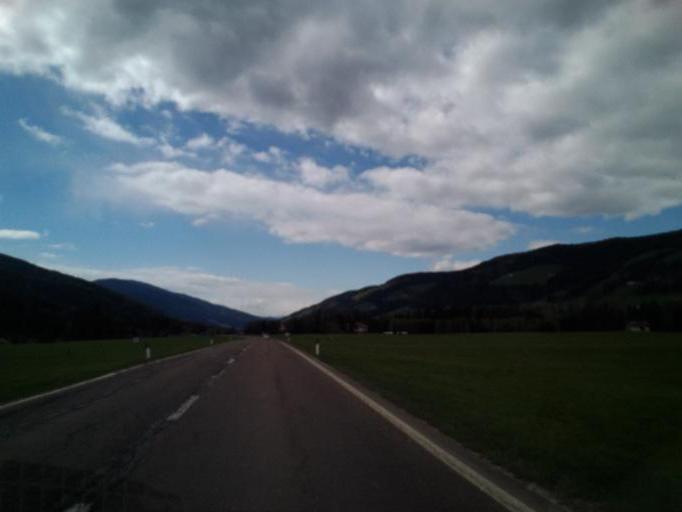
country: IT
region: Trentino-Alto Adige
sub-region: Bolzano
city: Dobbiaco
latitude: 46.7297
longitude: 12.2155
